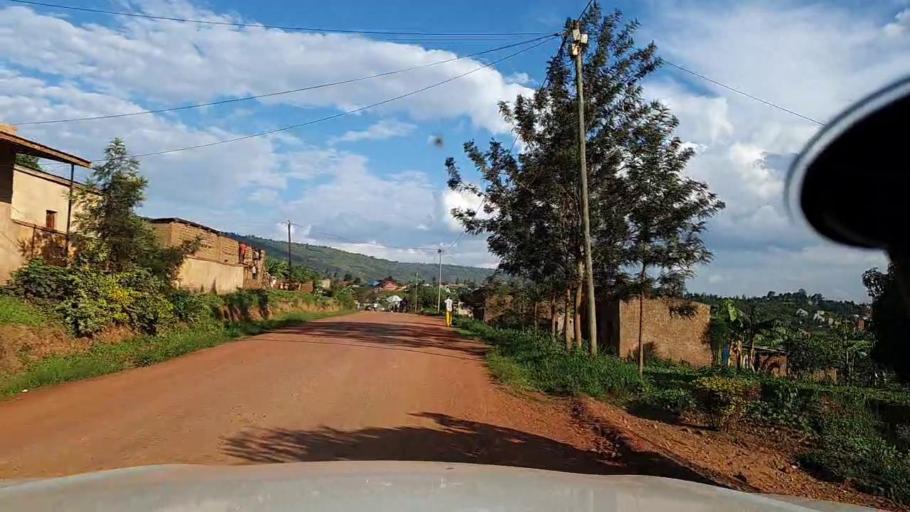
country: RW
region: Kigali
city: Kigali
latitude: -1.8933
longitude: 29.9604
